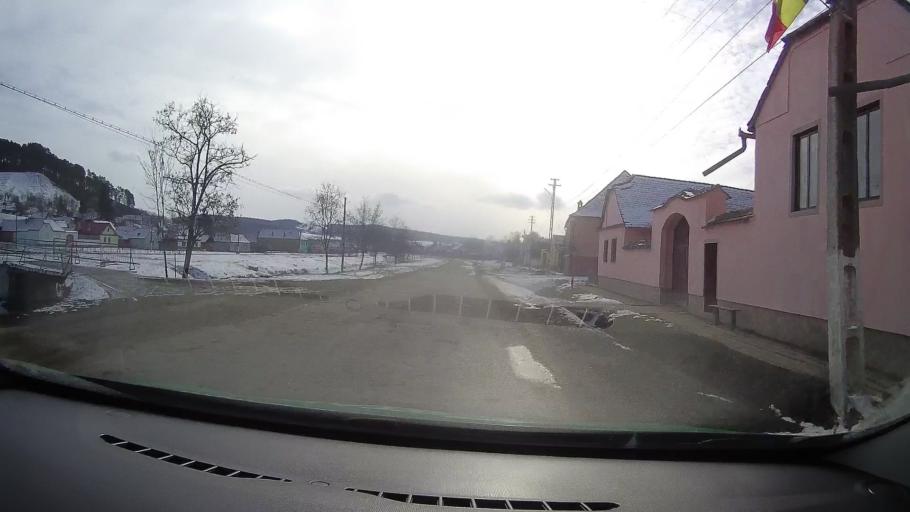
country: RO
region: Sibiu
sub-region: Comuna Bradeni
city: Bradeni
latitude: 46.0837
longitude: 24.8314
